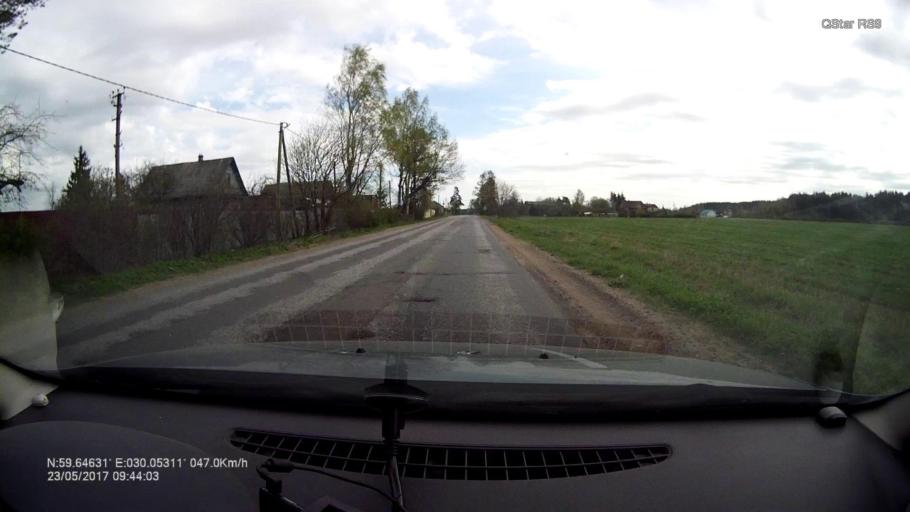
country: RU
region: Leningrad
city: Taytsy
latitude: 59.6463
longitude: 30.0531
